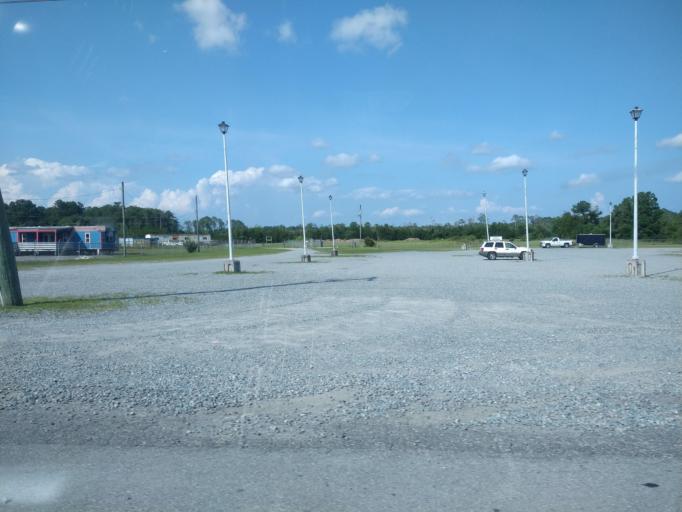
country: US
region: North Carolina
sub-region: Onslow County
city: Piney Green
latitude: 34.7360
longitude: -77.3554
